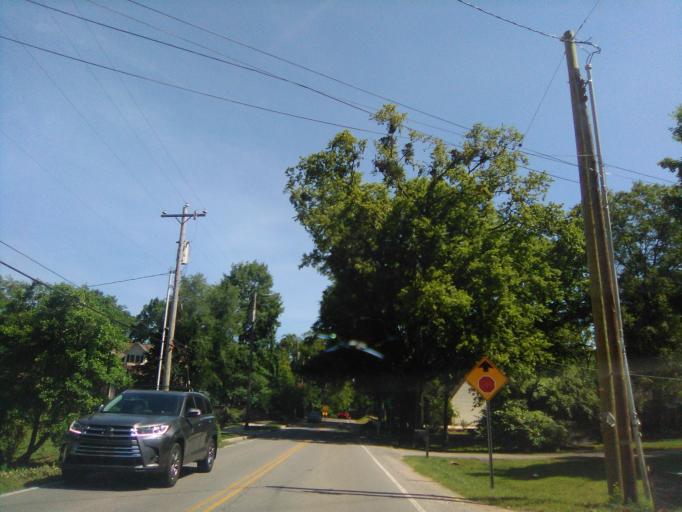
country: US
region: Tennessee
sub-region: Davidson County
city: Belle Meade
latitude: 36.1234
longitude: -86.8354
